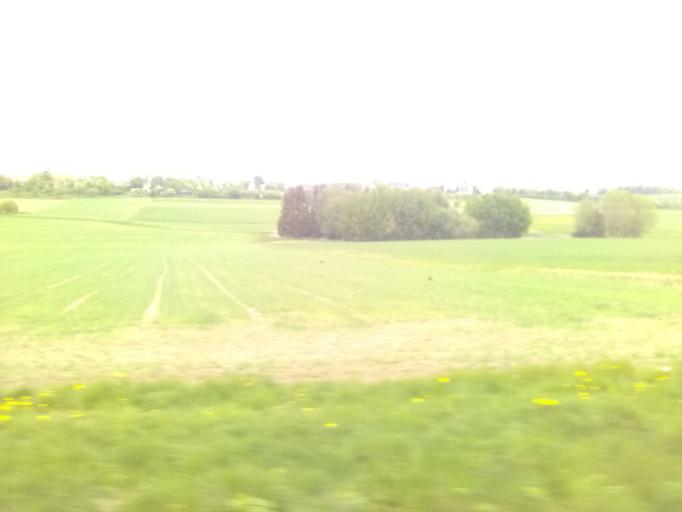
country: DE
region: Bavaria
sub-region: Regierungsbezirk Mittelfranken
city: Kalchreuth
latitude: 49.5523
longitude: 11.1348
